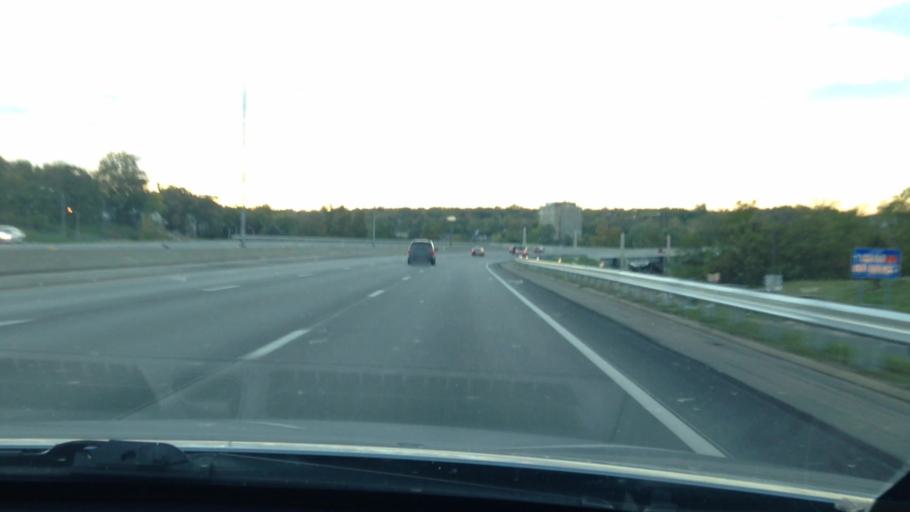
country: US
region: Kansas
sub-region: Johnson County
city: Westwood
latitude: 39.0384
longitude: -94.5565
